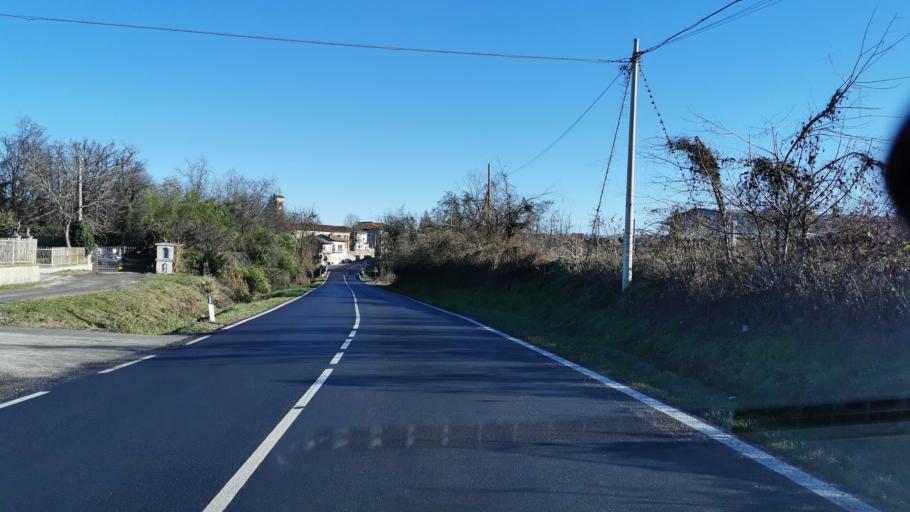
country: IT
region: Piedmont
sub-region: Provincia di Cuneo
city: Magliano Alpi
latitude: 44.4715
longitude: 7.8447
